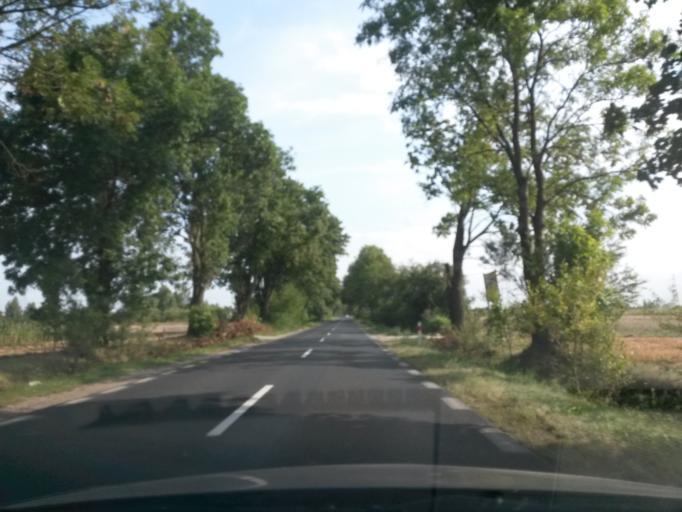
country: PL
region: Masovian Voivodeship
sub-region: Powiat sierpecki
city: Sierpc
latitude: 52.8745
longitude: 19.6597
